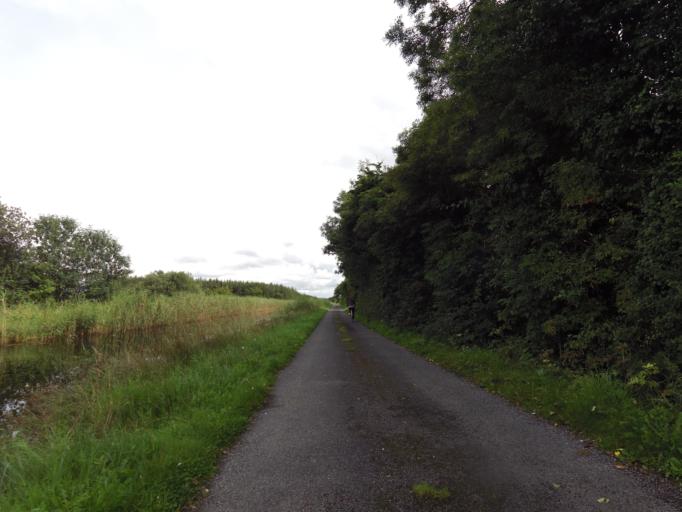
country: IE
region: Leinster
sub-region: An Longfort
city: Edgeworthstown
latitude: 53.5690
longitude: -7.5154
